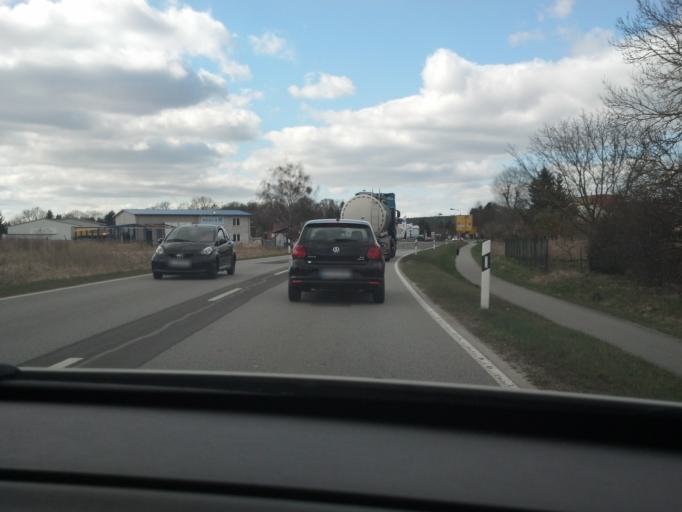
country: DE
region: Mecklenburg-Vorpommern
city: Wesenberg
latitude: 53.2788
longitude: 12.9697
